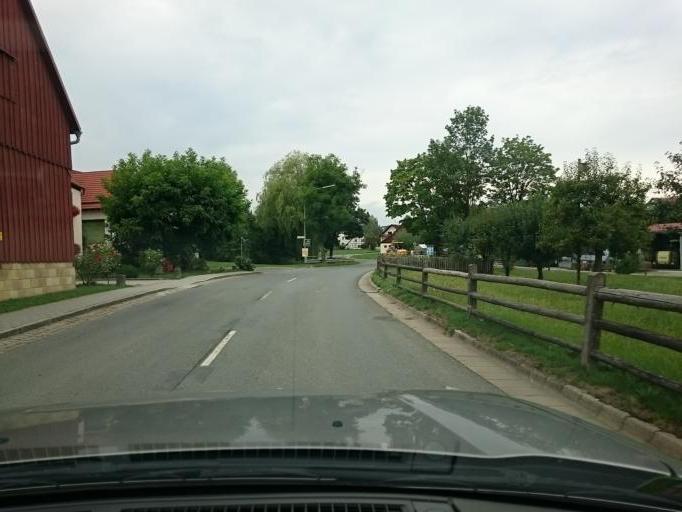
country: DE
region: Bavaria
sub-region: Regierungsbezirk Mittelfranken
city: Velden
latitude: 49.6666
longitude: 11.4652
